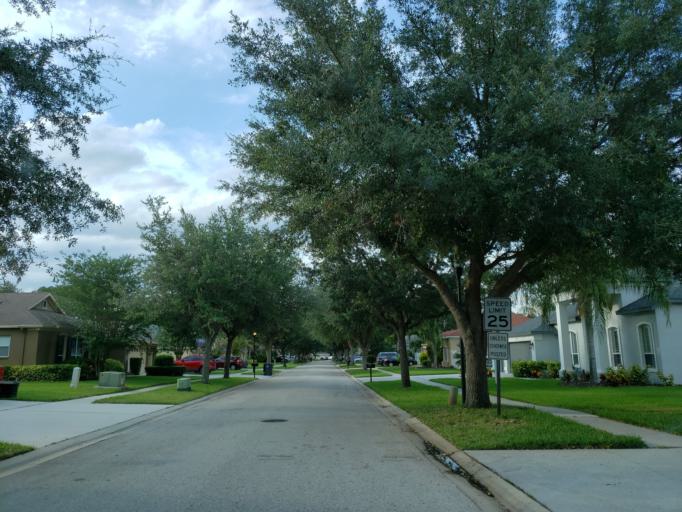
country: US
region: Florida
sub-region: Hillsborough County
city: Fish Hawk
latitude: 27.8469
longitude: -82.2294
